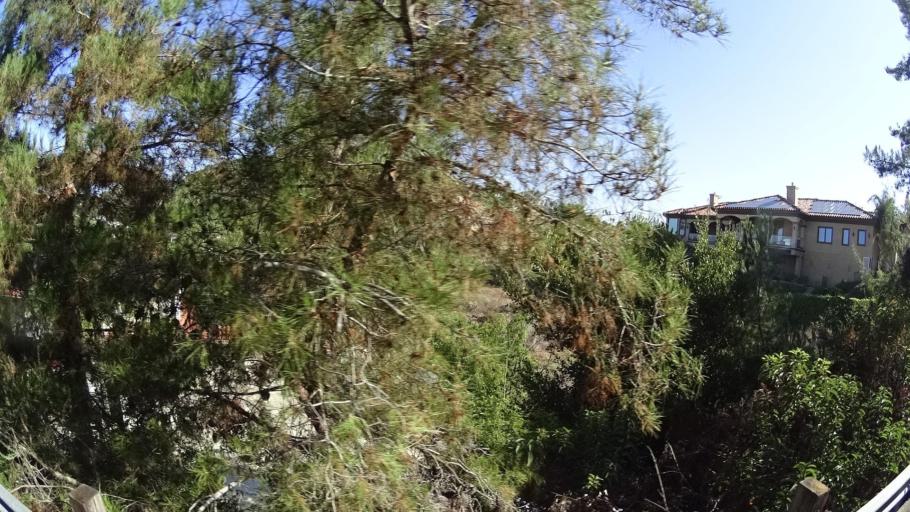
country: US
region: California
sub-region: San Diego County
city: Casa de Oro-Mount Helix
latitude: 32.7691
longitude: -116.9914
